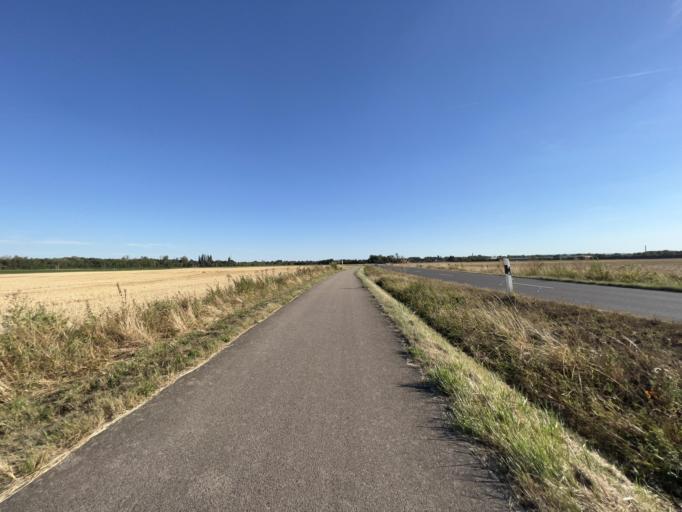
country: DE
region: North Rhine-Westphalia
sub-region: Regierungsbezirk Koln
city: Dueren
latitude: 50.8275
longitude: 6.4917
